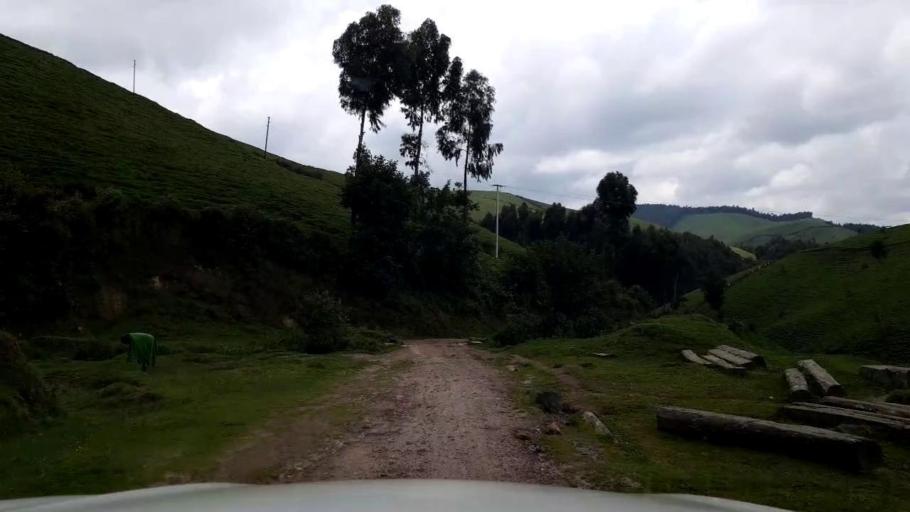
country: RW
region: Western Province
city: Gisenyi
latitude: -1.6831
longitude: 29.4178
